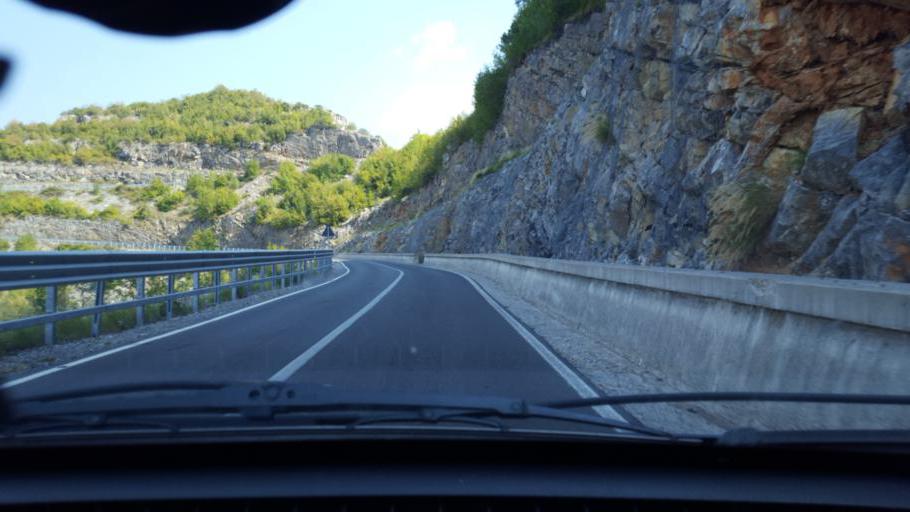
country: AL
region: Shkoder
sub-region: Rrethi i Malesia e Madhe
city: Kastrat
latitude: 42.4133
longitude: 19.5018
